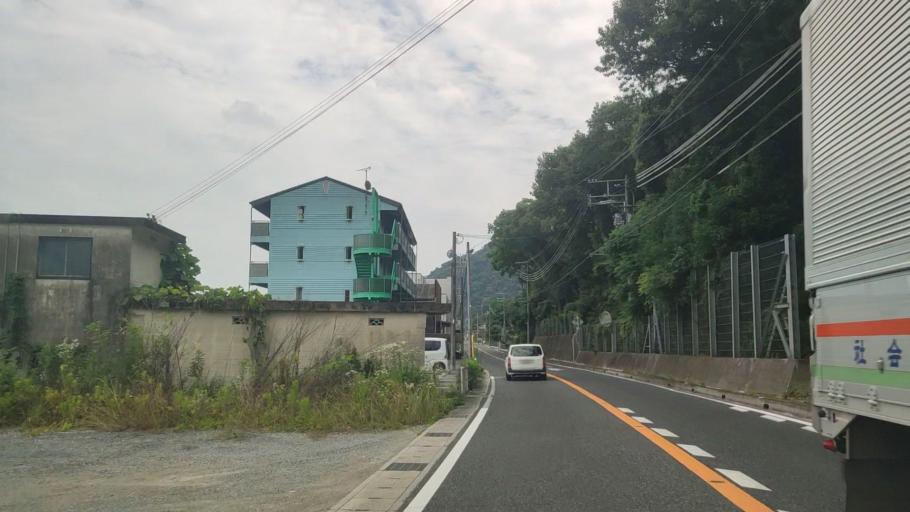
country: JP
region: Hyogo
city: Tatsunocho-tominaga
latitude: 34.8825
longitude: 134.5461
